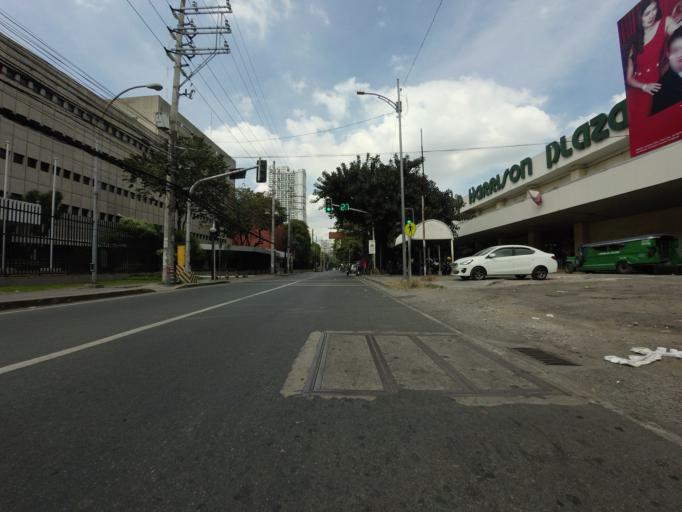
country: PH
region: Metro Manila
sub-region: City of Manila
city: Port Area
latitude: 14.5618
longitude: 120.9886
